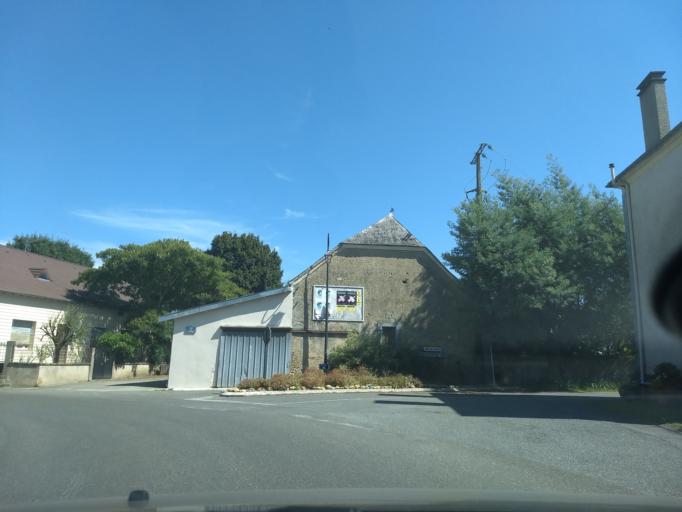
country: FR
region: Aquitaine
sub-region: Departement des Pyrenees-Atlantiques
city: Soumoulou
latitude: 43.2746
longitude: -0.1822
